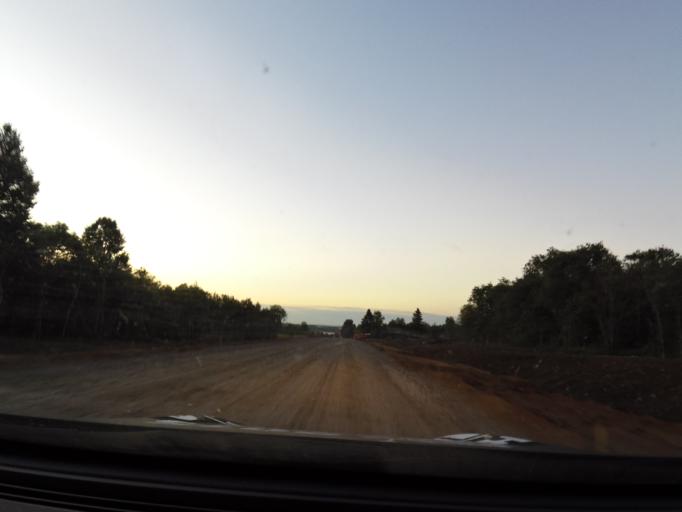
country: RU
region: Vologda
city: Vytegra
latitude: 61.0006
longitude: 36.1279
